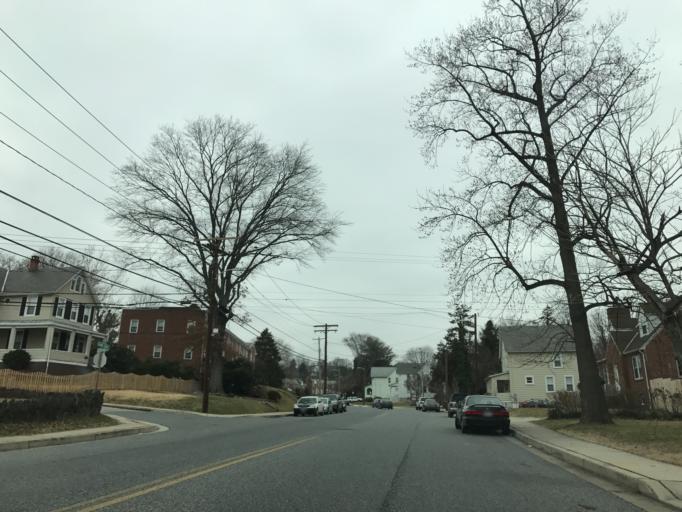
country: US
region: Maryland
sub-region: Baltimore County
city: Overlea
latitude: 39.3399
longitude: -76.5427
